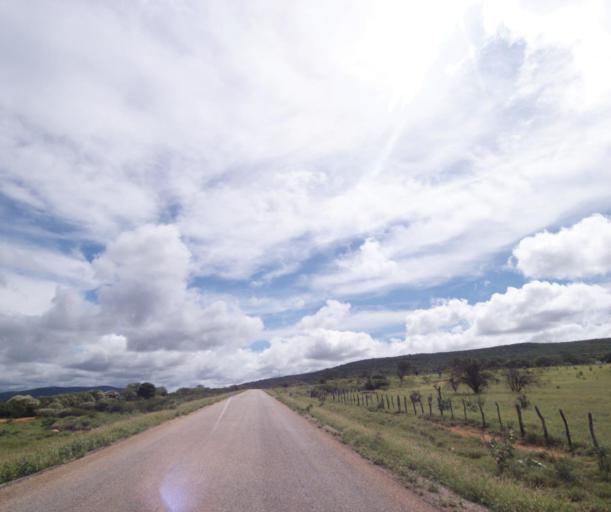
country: BR
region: Bahia
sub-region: Brumado
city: Brumado
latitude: -14.2100
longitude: -41.6294
